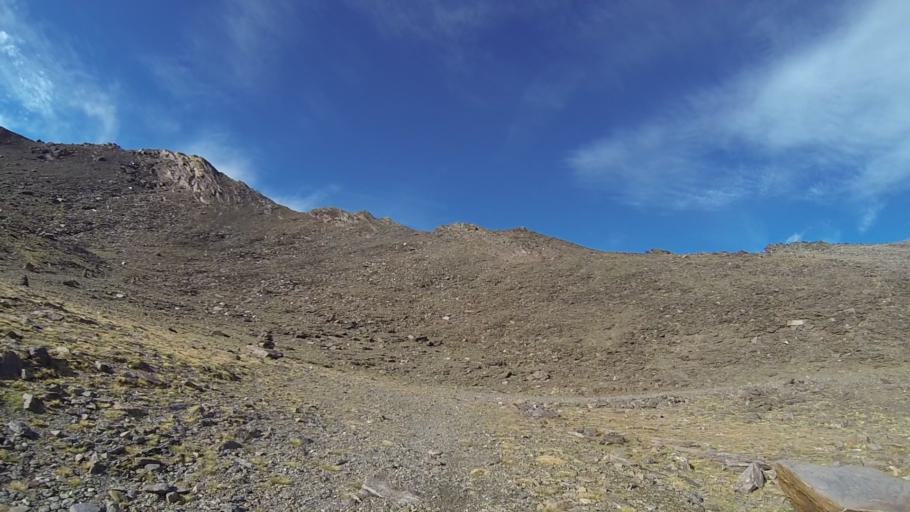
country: ES
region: Andalusia
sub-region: Provincia de Granada
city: Trevelez
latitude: 37.0543
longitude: -3.3245
